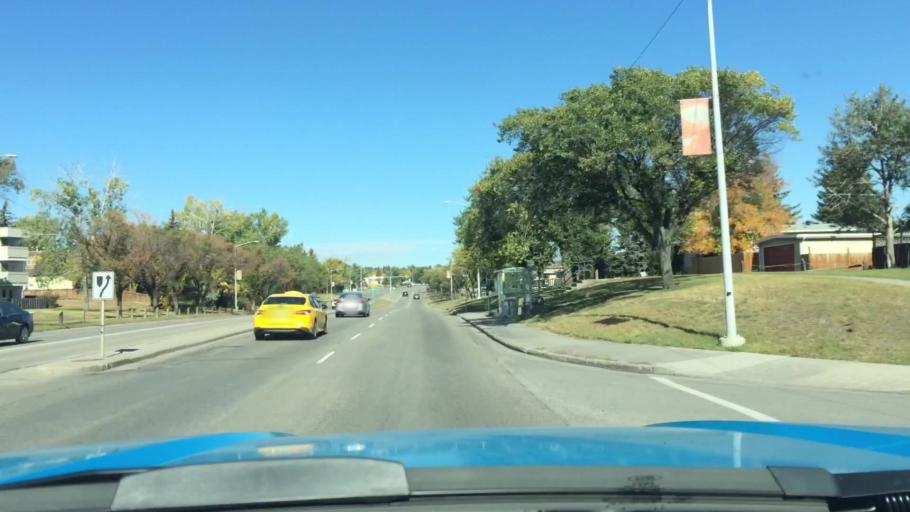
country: CA
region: Alberta
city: Calgary
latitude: 51.1135
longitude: -114.0645
